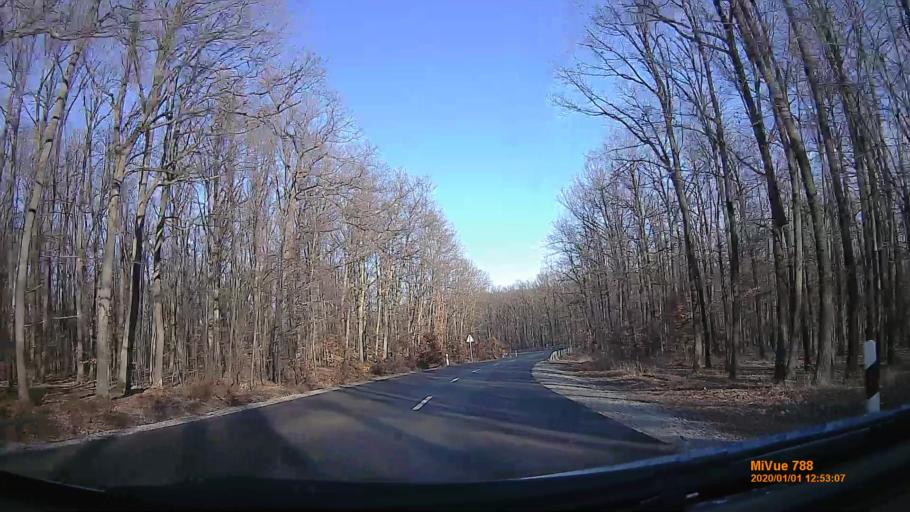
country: HU
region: Heves
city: Paradsasvar
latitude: 47.9035
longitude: 19.9950
